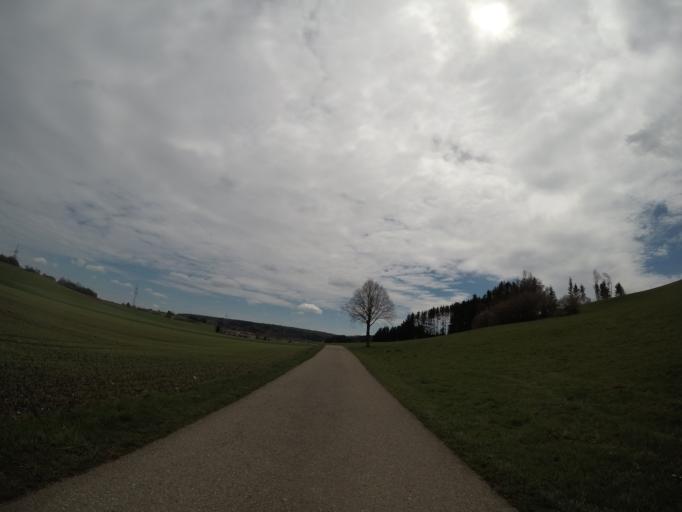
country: DE
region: Baden-Wuerttemberg
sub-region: Tuebingen Region
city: Westerheim
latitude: 48.5036
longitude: 9.6459
